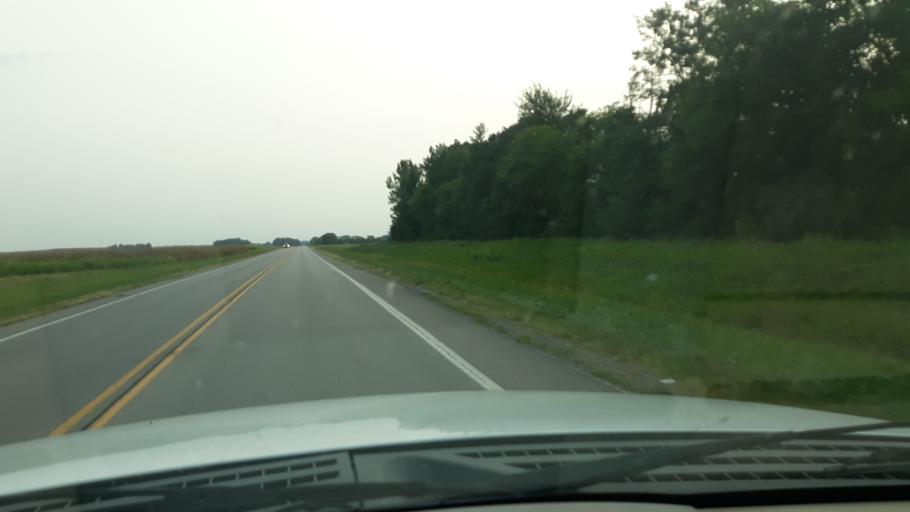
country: US
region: Illinois
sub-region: White County
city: Carmi
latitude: 38.1399
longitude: -88.0896
